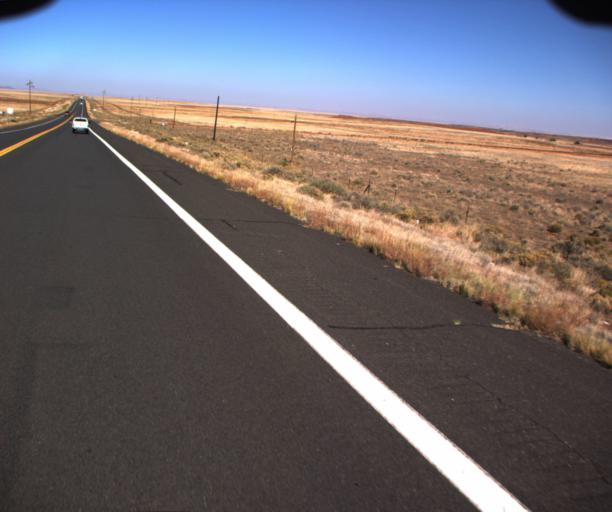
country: US
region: Arizona
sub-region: Coconino County
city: Flagstaff
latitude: 35.6573
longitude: -111.5140
